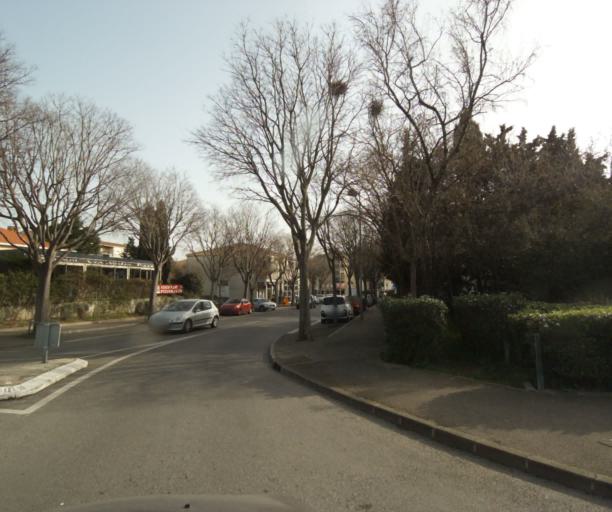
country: FR
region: Provence-Alpes-Cote d'Azur
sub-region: Departement des Bouches-du-Rhone
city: Les Pennes-Mirabeau
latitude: 43.4269
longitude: 5.2781
